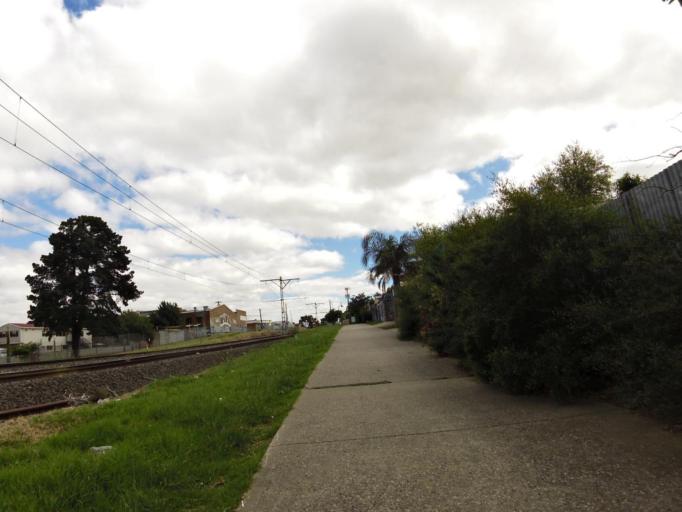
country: AU
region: Victoria
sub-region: Moreland
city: Coburg North
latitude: -37.7286
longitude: 144.9623
